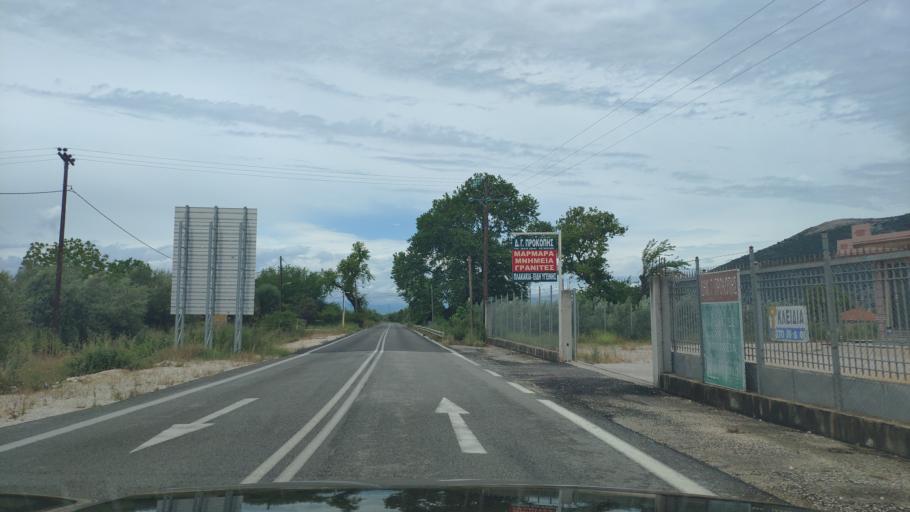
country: GR
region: West Greece
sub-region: Nomos Aitolias kai Akarnanias
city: Vonitsa
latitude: 38.8942
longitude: 20.8998
